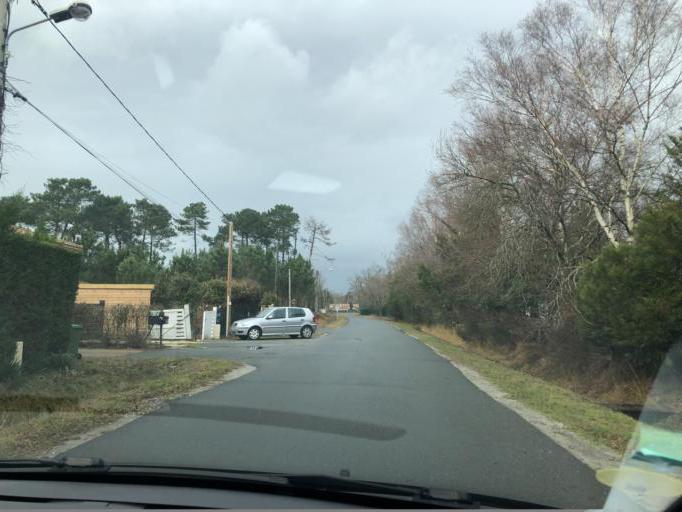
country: FR
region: Aquitaine
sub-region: Departement de la Gironde
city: Hourtin
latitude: 45.1792
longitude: -1.0750
